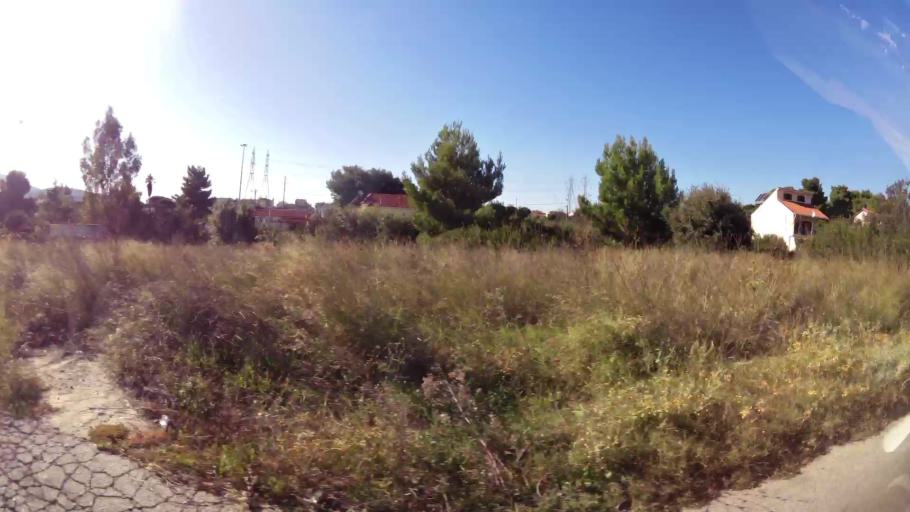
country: GR
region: Attica
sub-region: Nomarchia Anatolikis Attikis
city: Gerakas
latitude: 38.0174
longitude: 23.8678
